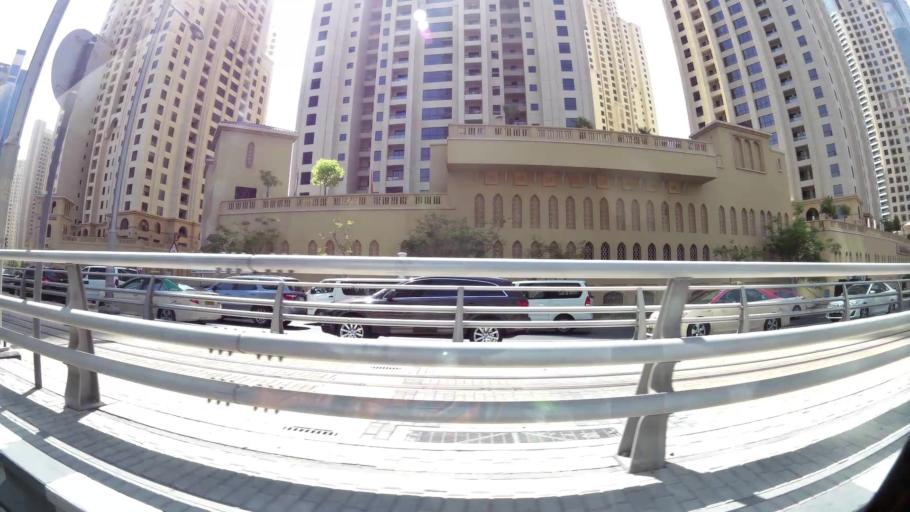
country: AE
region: Dubai
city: Dubai
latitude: 25.0767
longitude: 55.1362
